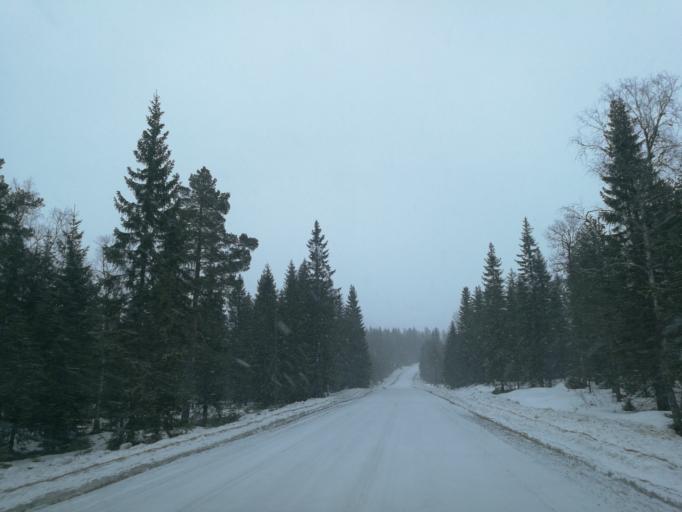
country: SE
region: Vaermland
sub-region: Torsby Kommun
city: Torsby
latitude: 60.6486
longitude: 12.9190
